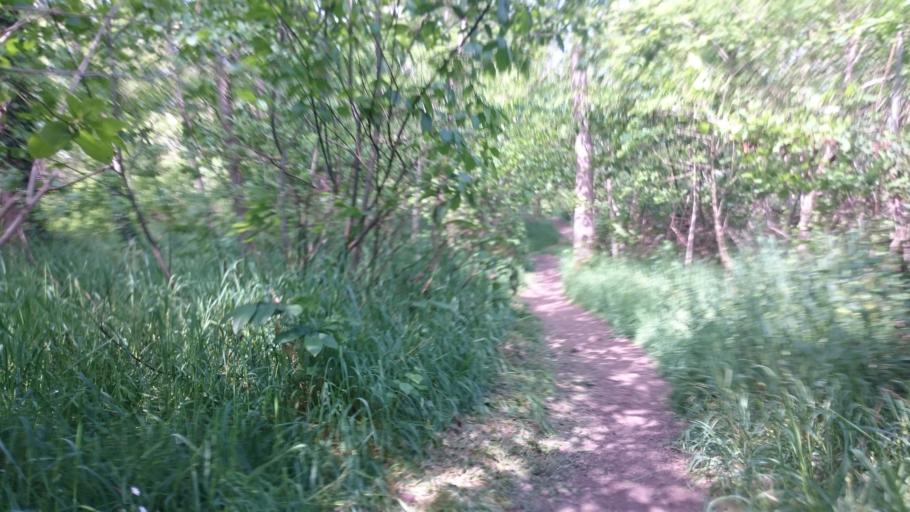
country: FR
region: Pays de la Loire
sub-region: Departement de la Loire-Atlantique
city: Bouguenais
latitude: 47.1814
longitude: -1.6414
